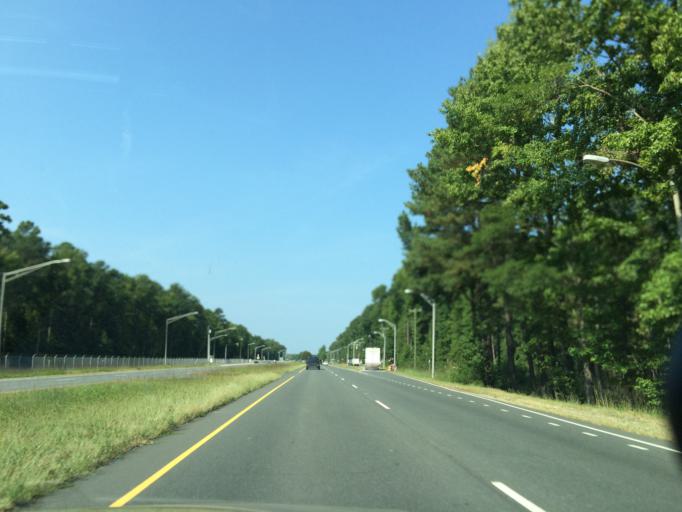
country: US
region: Virginia
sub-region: King George County
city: Dahlgren
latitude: 38.3579
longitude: -77.0285
